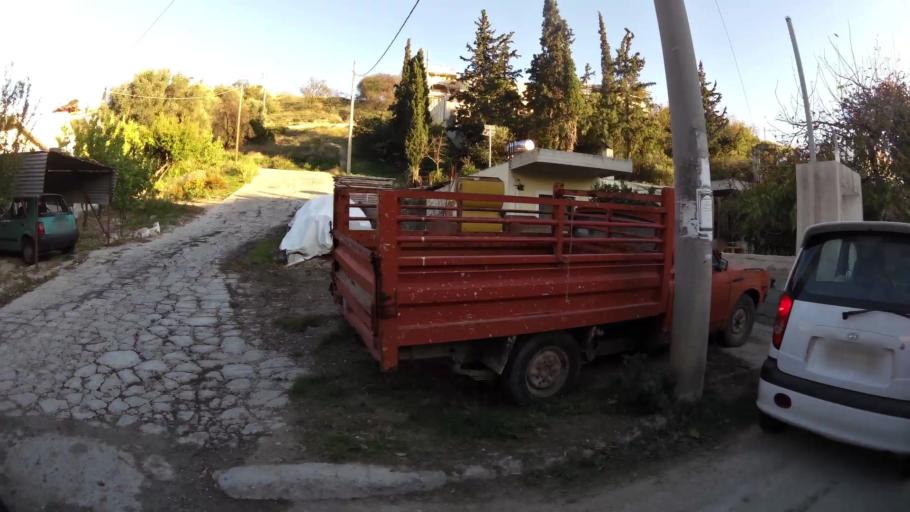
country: GR
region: Attica
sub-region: Nomarchia Anatolikis Attikis
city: Spata
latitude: 37.9657
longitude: 23.9096
